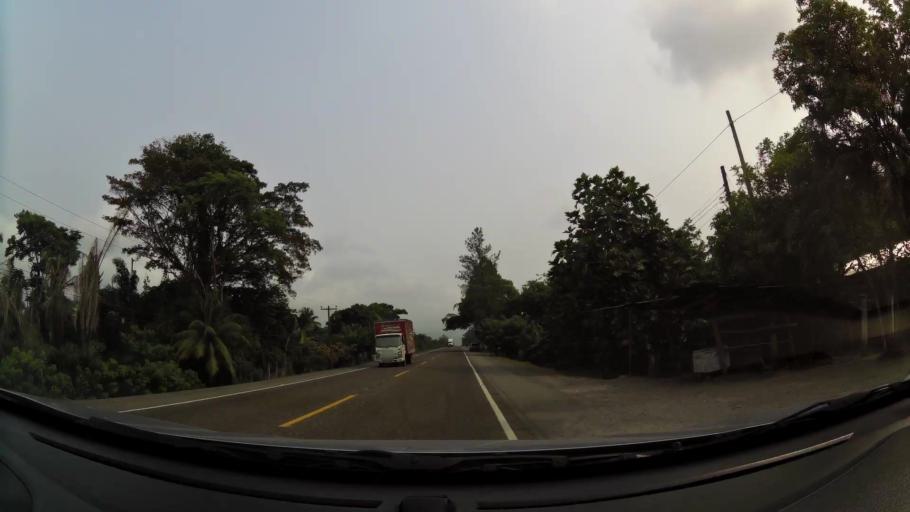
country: HN
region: Atlantida
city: Mezapa
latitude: 15.6059
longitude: -87.6118
